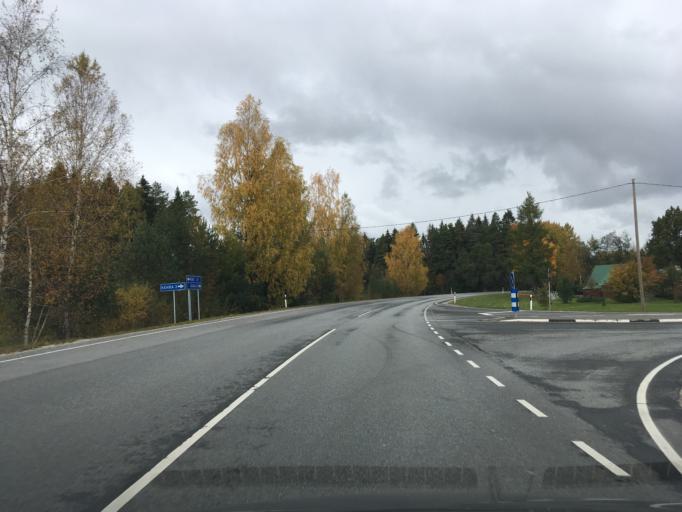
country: EE
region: Harju
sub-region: Anija vald
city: Kehra
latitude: 59.3119
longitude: 25.3446
